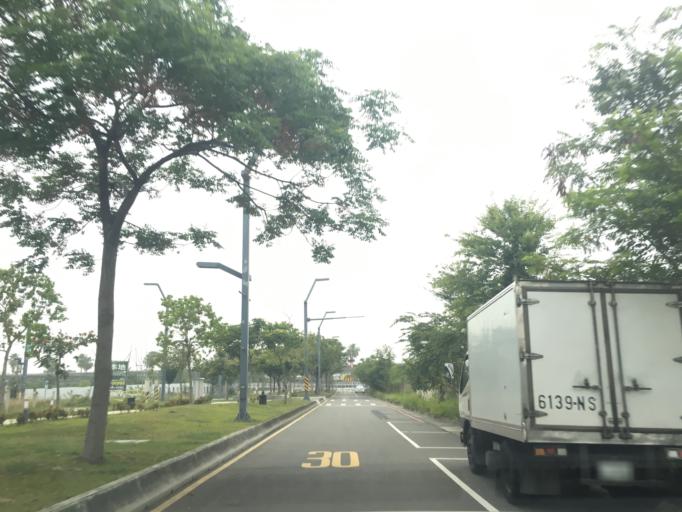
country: TW
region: Taiwan
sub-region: Taichung City
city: Taichung
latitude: 24.1936
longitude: 120.6471
